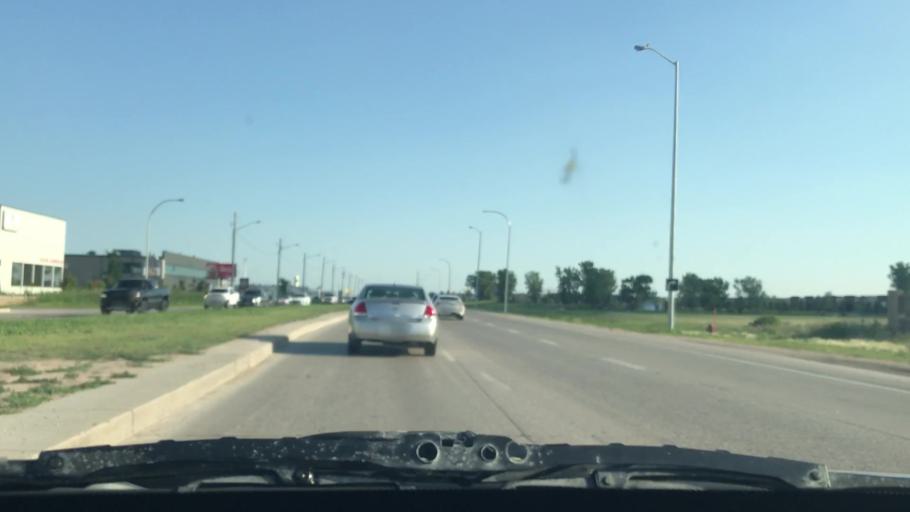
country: CA
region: Manitoba
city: Winnipeg
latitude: 49.8381
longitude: -97.2092
